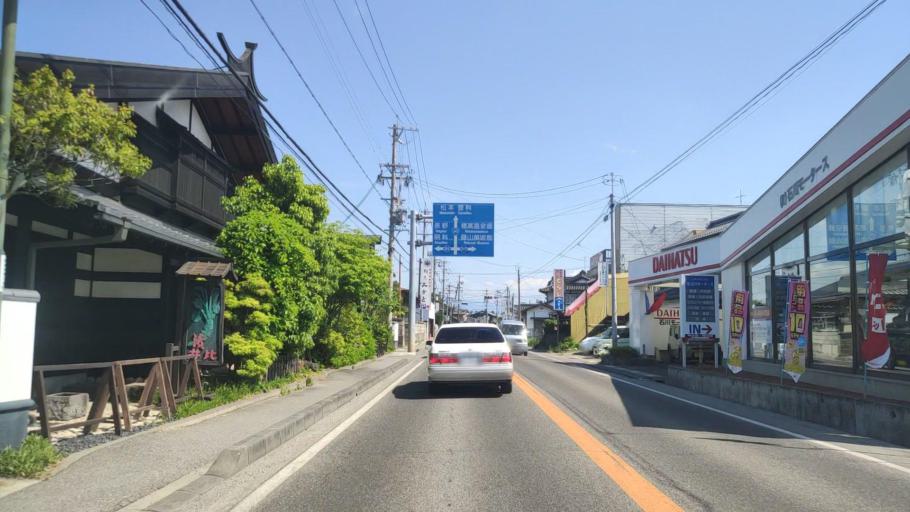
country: JP
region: Nagano
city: Hotaka
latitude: 36.3461
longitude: 137.8852
